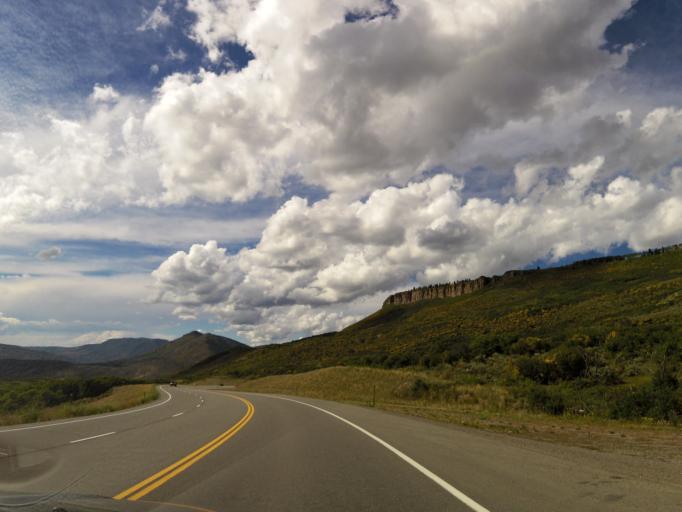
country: US
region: Colorado
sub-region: Hinsdale County
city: Lake City
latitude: 38.3932
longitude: -107.4450
